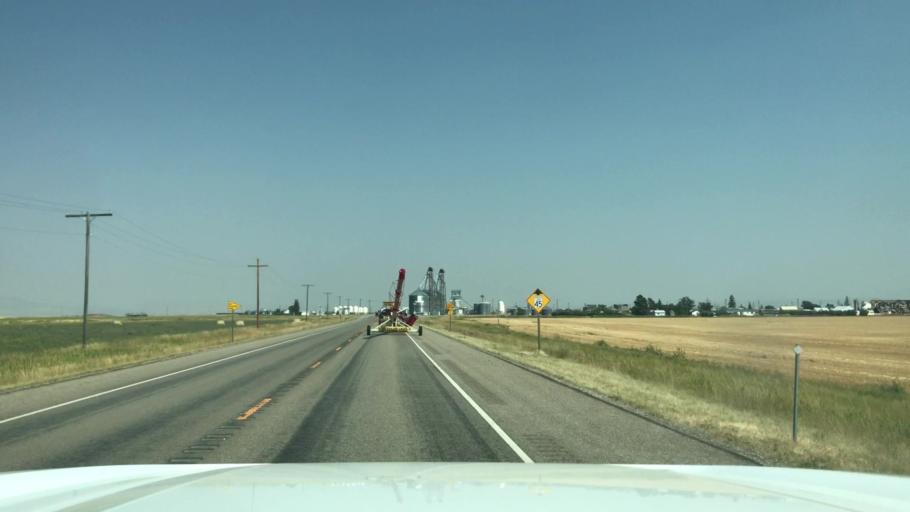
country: US
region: Montana
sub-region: Judith Basin County
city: Stanford
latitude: 47.0552
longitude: -109.9197
